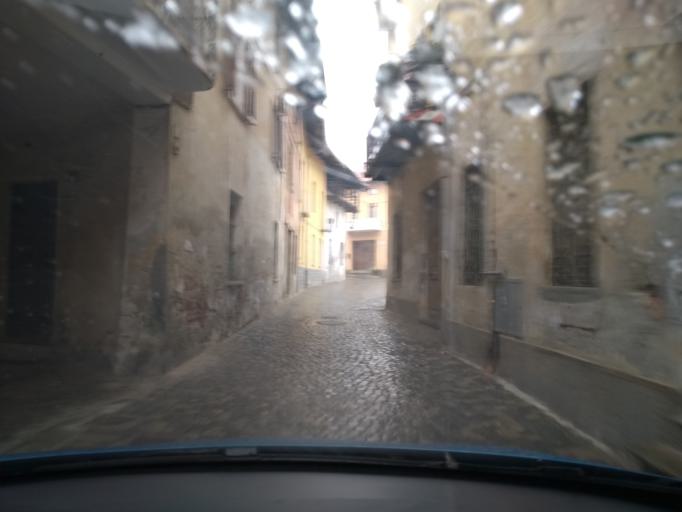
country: IT
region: Piedmont
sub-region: Provincia di Torino
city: Balangero
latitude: 45.2741
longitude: 7.5203
